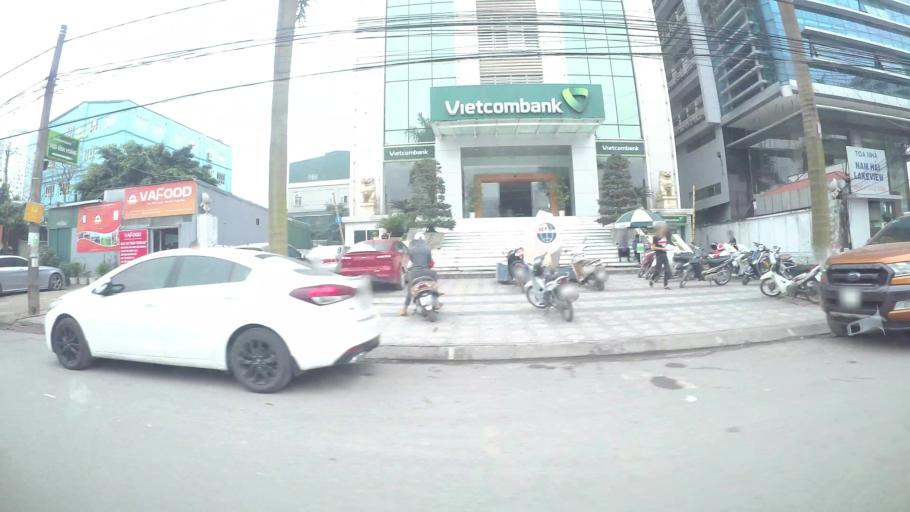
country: VN
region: Ha Noi
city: Hai BaTrung
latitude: 20.9837
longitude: 105.8675
